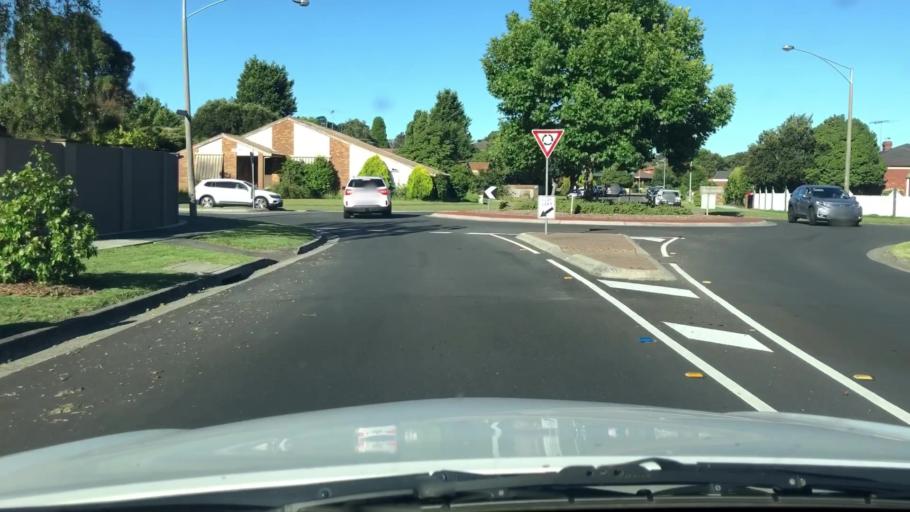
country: AU
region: Victoria
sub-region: Knox
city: Rowville
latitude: -37.9291
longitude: 145.2410
